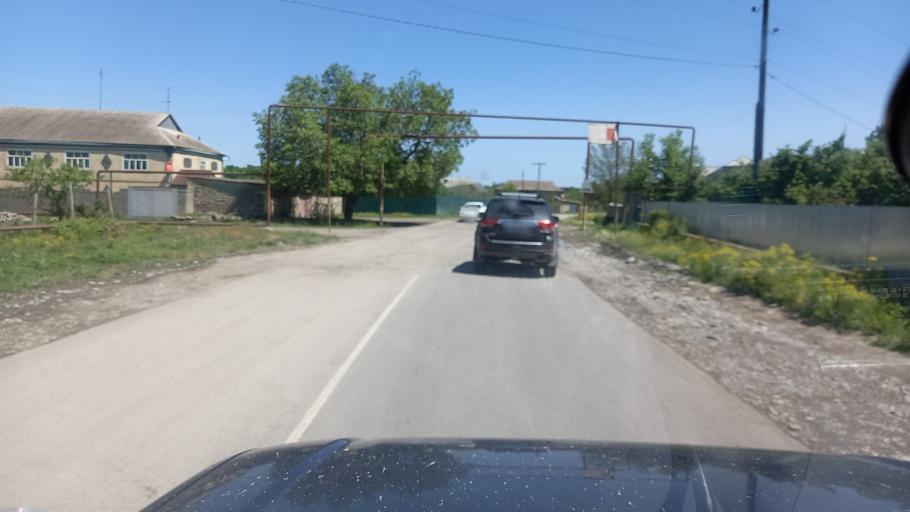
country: RU
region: Dagestan
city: Samur
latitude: 41.8091
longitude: 48.5167
